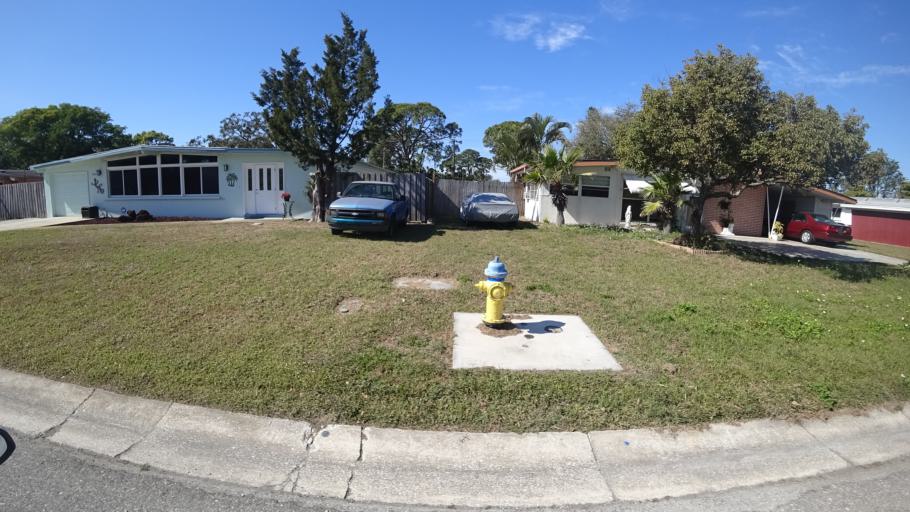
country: US
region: Florida
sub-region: Manatee County
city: South Bradenton
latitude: 27.4599
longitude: -82.6200
